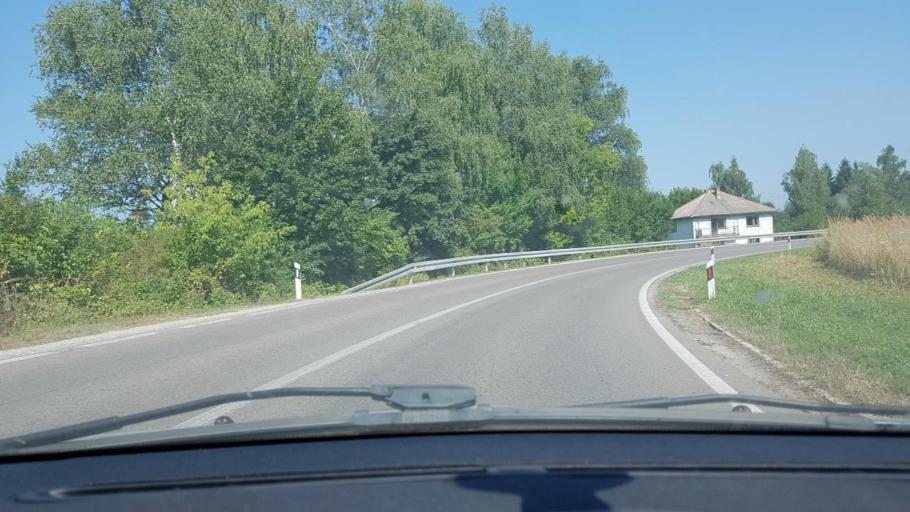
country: BA
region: Federation of Bosnia and Herzegovina
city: Mala Kladusa
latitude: 45.1526
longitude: 15.8293
